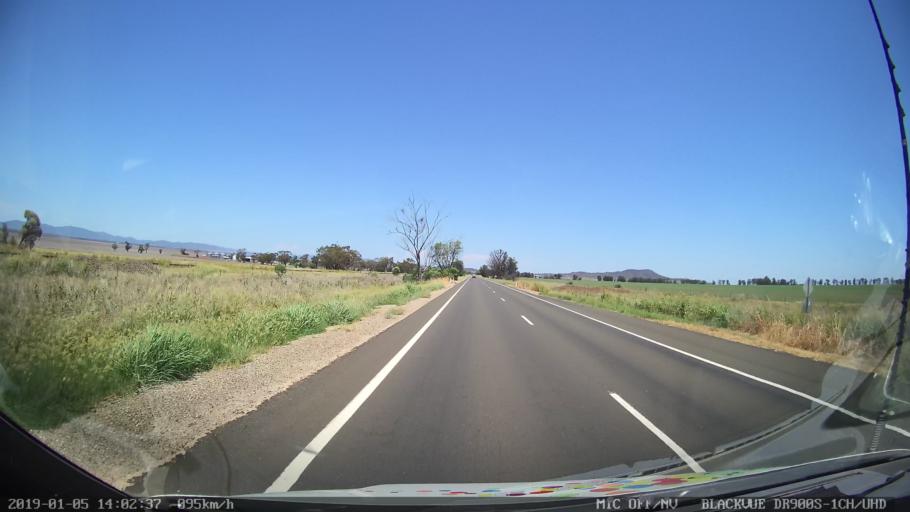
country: AU
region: New South Wales
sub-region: Gunnedah
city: Gunnedah
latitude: -31.1814
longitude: 150.3400
